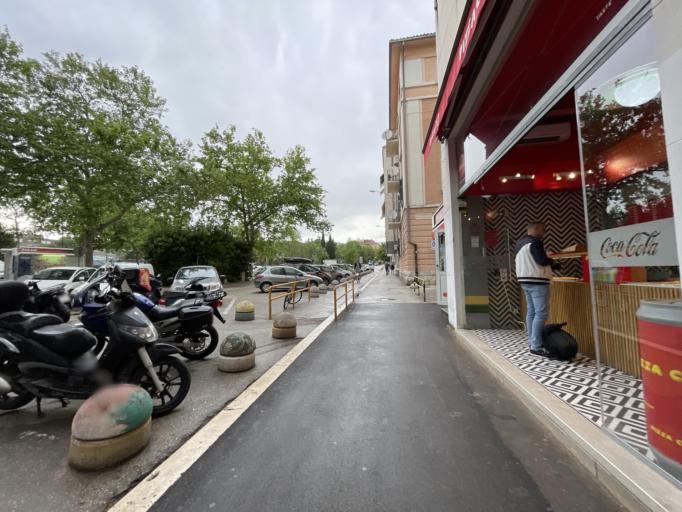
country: HR
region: Splitsko-Dalmatinska
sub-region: Grad Split
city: Split
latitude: 43.5119
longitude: 16.4363
